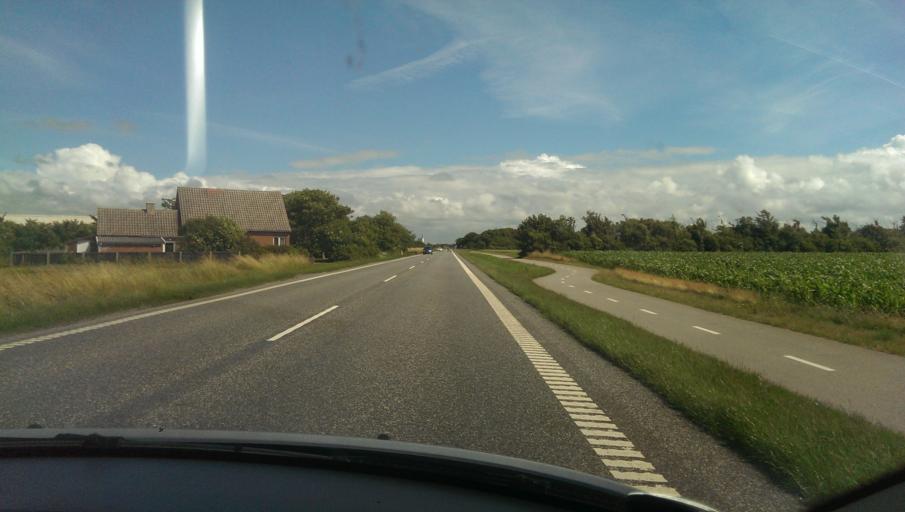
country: DK
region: Central Jutland
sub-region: Ringkobing-Skjern Kommune
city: Ringkobing
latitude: 56.1068
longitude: 8.2053
